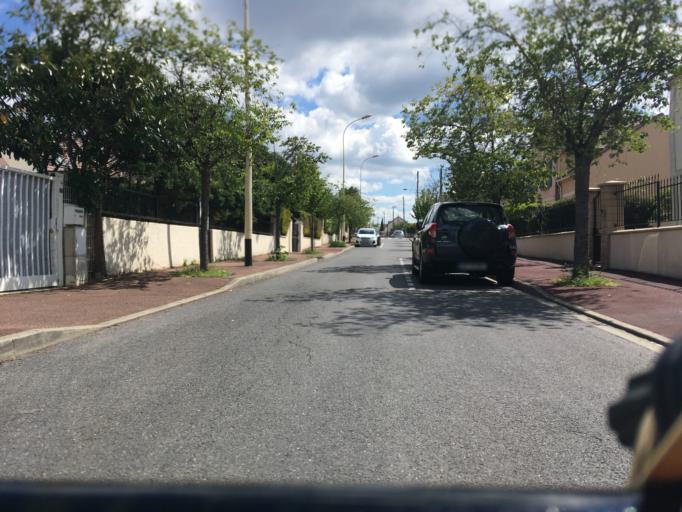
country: FR
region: Ile-de-France
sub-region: Departement des Yvelines
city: Montesson
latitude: 48.9089
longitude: 2.1399
